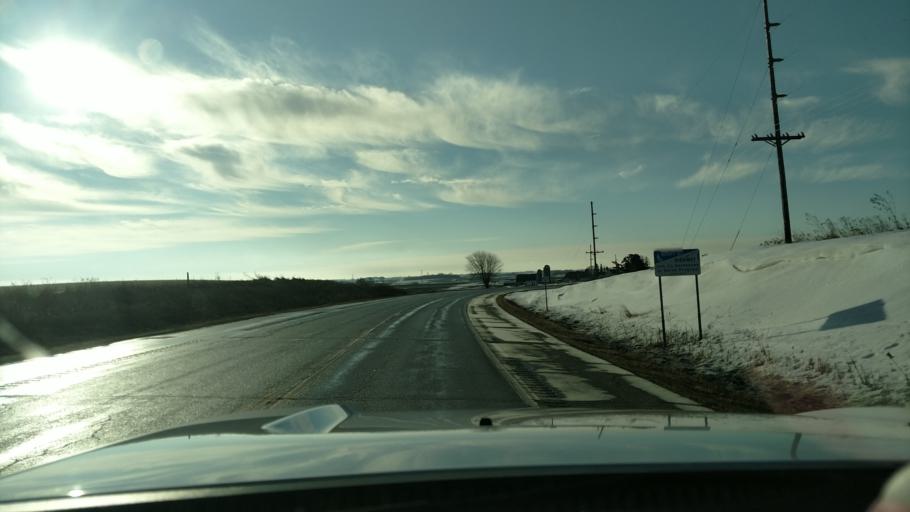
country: US
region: Minnesota
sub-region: Olmsted County
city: Oronoco
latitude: 44.1934
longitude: -92.4207
